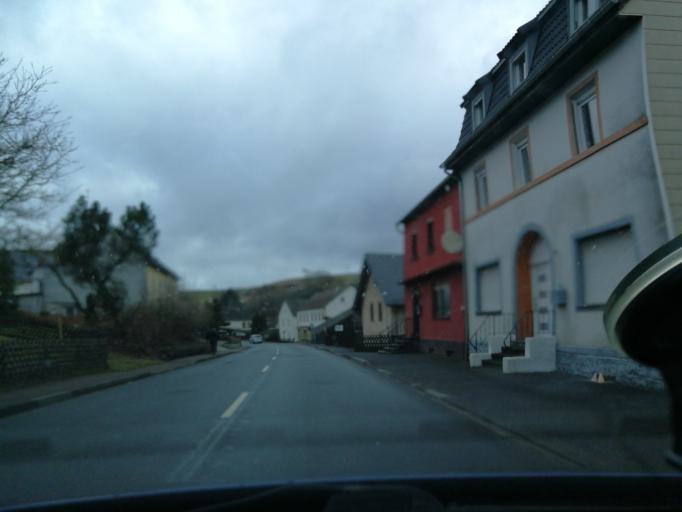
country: DE
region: Rheinland-Pfalz
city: Dreis-Bruck
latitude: 50.2640
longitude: 6.7915
